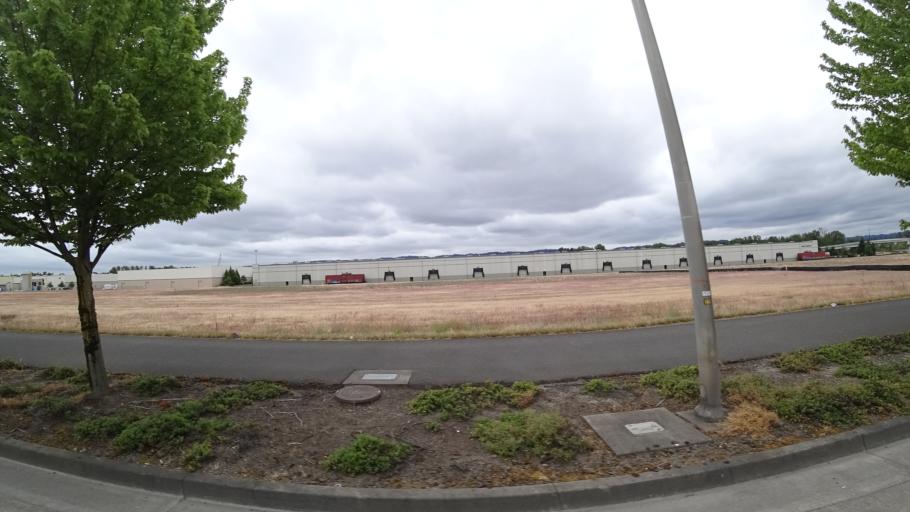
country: US
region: Washington
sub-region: Clark County
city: Lake Shore
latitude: 45.6346
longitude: -122.7532
